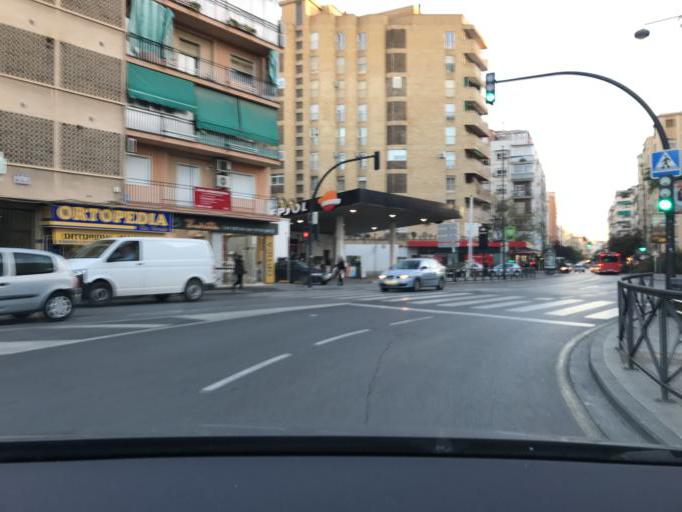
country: ES
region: Andalusia
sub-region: Provincia de Granada
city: Armilla
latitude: 37.1611
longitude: -3.5997
